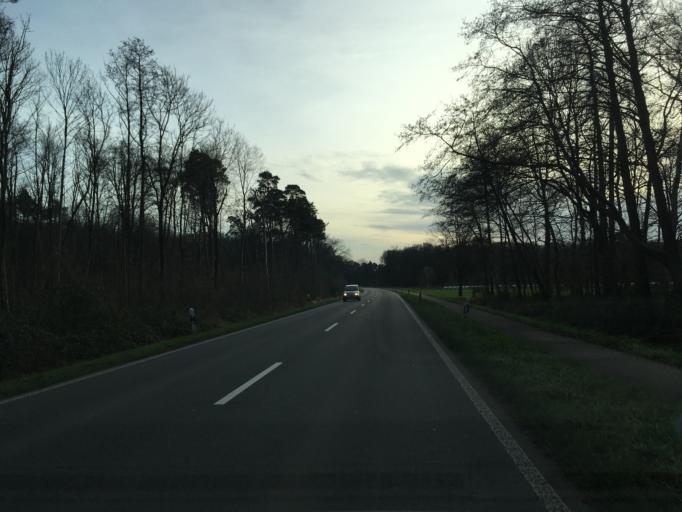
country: DE
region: North Rhine-Westphalia
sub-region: Regierungsbezirk Munster
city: Ahaus
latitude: 52.0306
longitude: 7.0242
